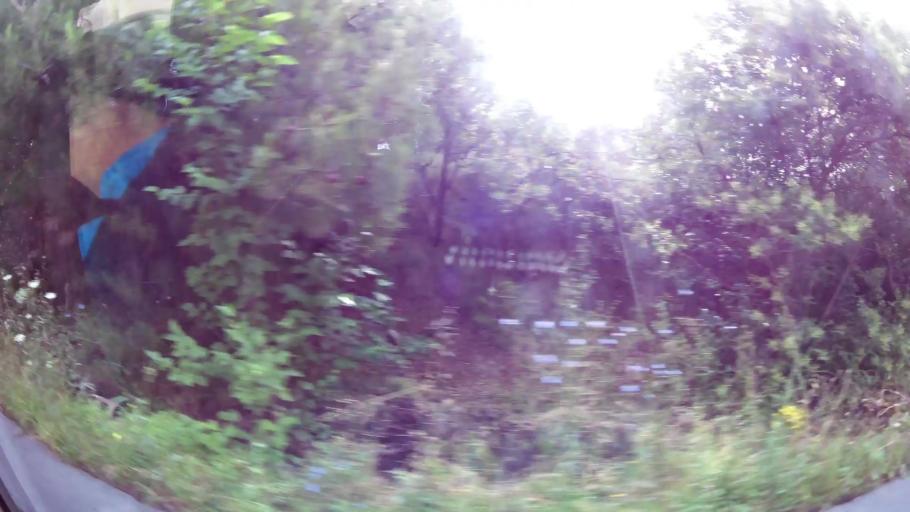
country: GR
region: Central Macedonia
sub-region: Nomos Thessalonikis
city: Panorama
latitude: 40.5773
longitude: 23.0264
